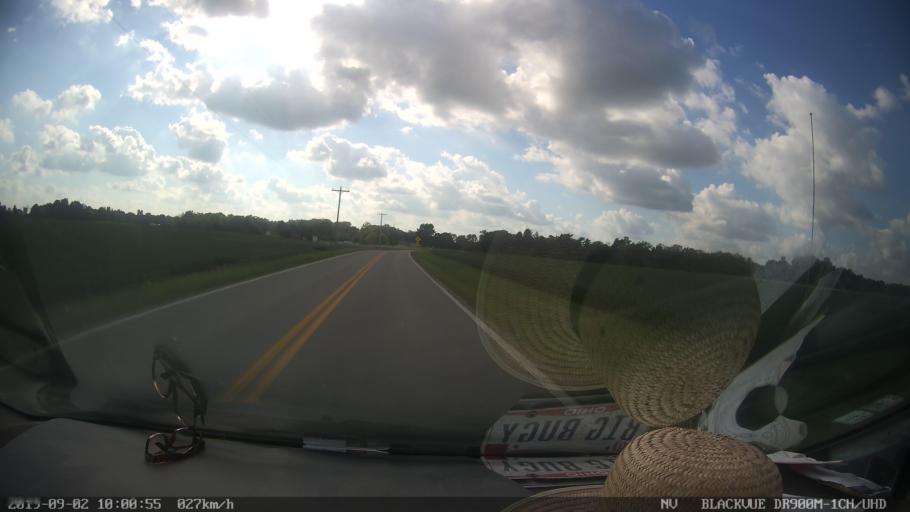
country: US
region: Ohio
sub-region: Delaware County
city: Ashley
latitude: 40.4543
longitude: -82.9532
